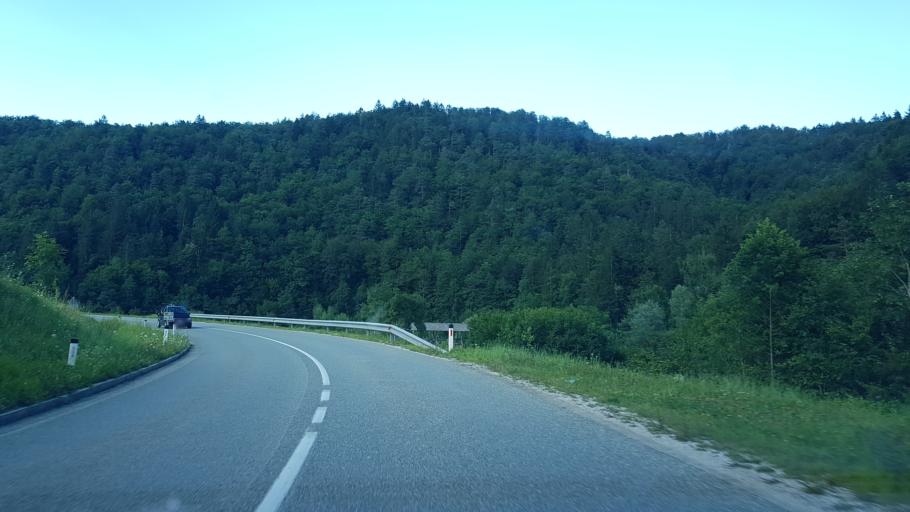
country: SI
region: Gorenja Vas-Poljane
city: Gorenja Vas
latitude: 46.0974
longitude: 14.1138
